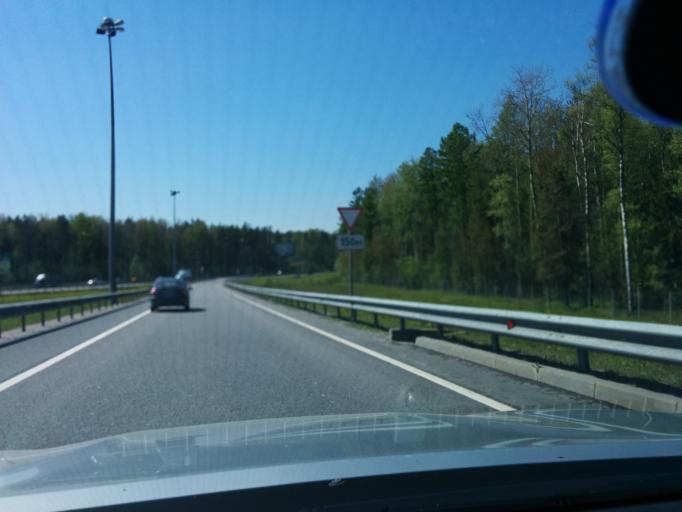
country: RU
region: St.-Petersburg
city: Krasnogvargeisky
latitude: 59.9472
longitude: 30.5386
